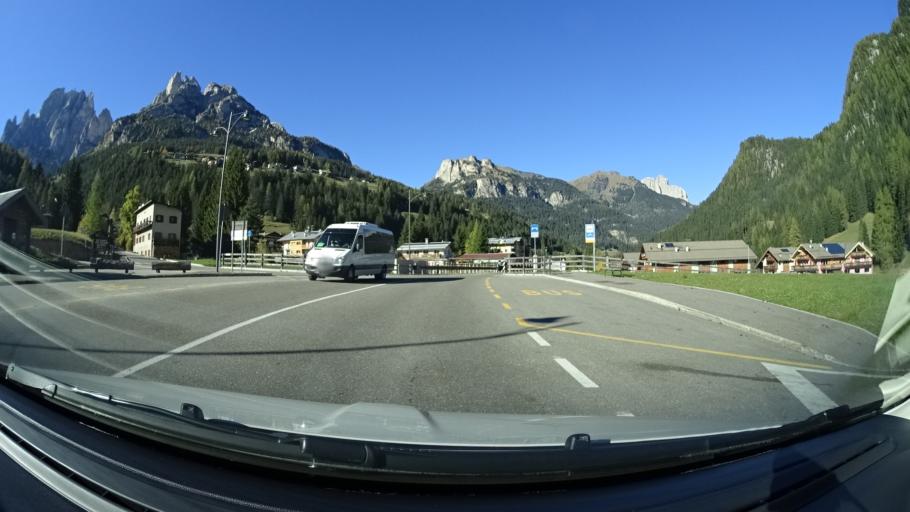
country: IT
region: Trentino-Alto Adige
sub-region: Provincia di Trento
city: Pozza di Fassa
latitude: 46.4417
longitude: 11.6956
